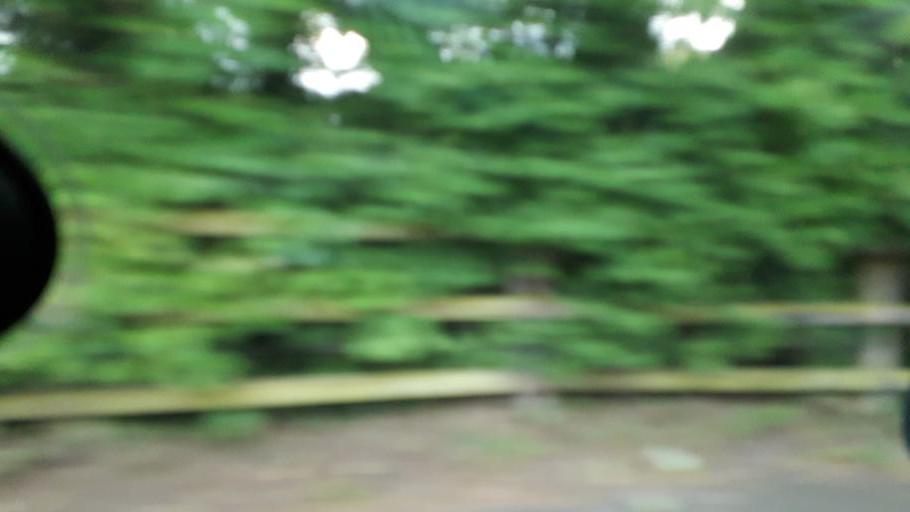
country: IE
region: Leinster
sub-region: Kildare
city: Celbridge
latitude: 53.3310
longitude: -6.5305
